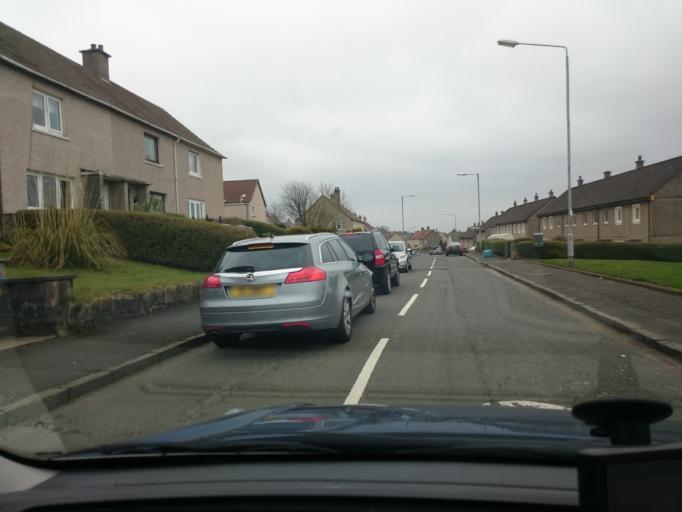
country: GB
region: Scotland
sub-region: North Lanarkshire
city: Kilsyth
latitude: 55.9829
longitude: -4.0685
